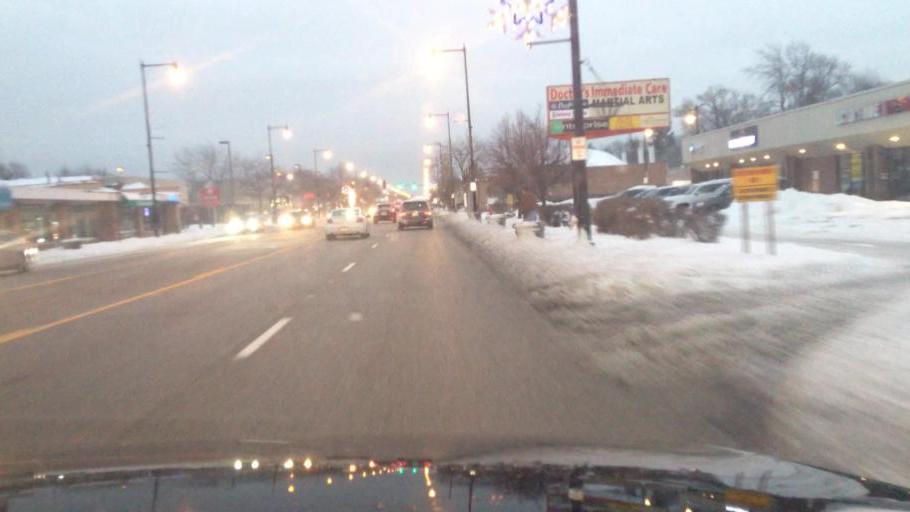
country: US
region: Illinois
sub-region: Cook County
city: Morton Grove
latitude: 42.0409
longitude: -87.7791
